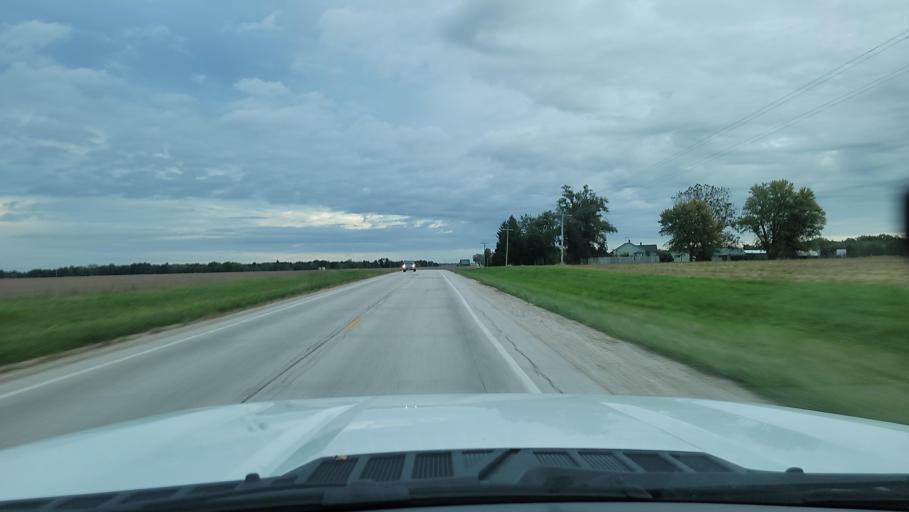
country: US
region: Illinois
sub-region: Schuyler County
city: Rushville
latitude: 40.0877
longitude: -90.6085
